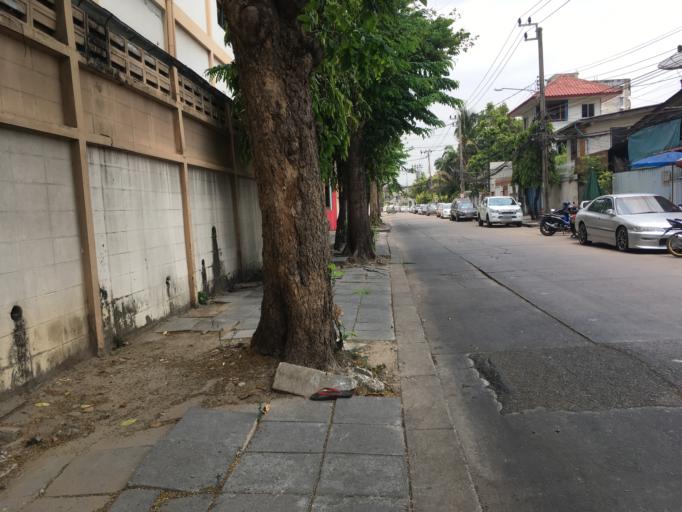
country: TH
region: Bangkok
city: Phaya Thai
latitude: 13.7911
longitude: 100.5446
